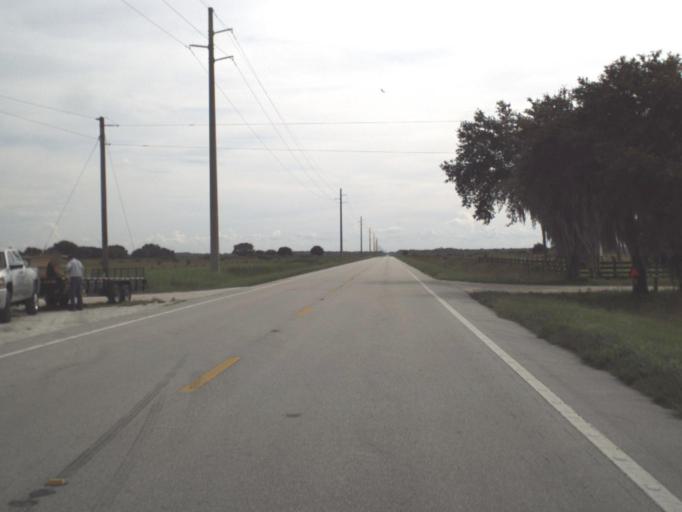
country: US
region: Florida
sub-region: Highlands County
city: Placid Lakes
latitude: 27.2091
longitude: -81.5389
